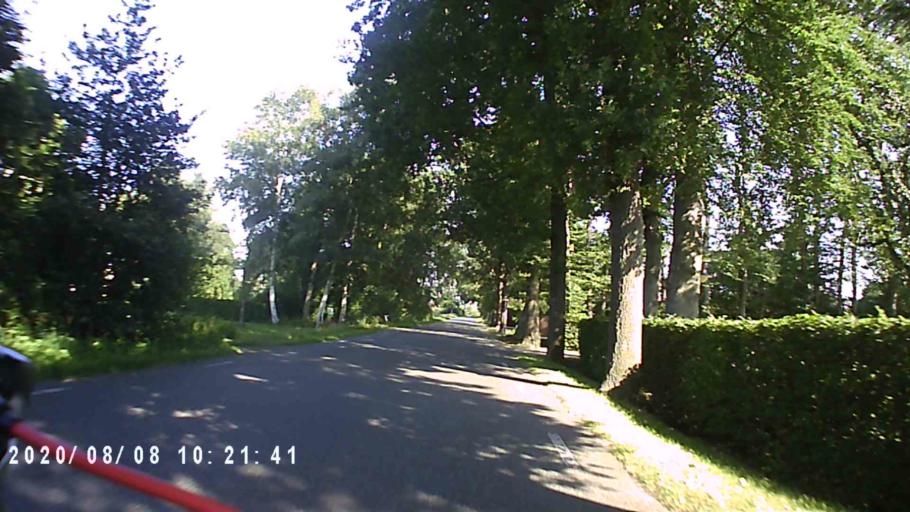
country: NL
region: Groningen
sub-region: Gemeente Leek
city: Leek
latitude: 53.1376
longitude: 6.3949
